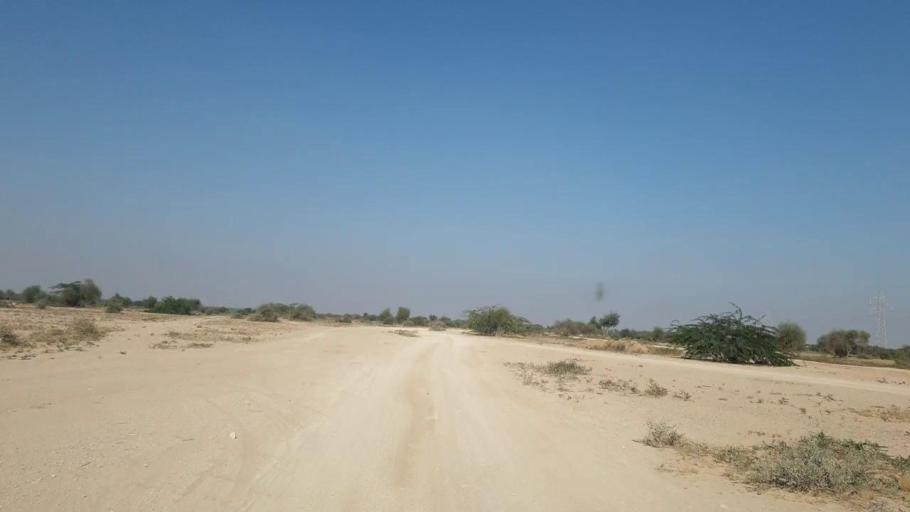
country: PK
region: Sindh
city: Jamshoro
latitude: 25.2929
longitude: 67.8138
